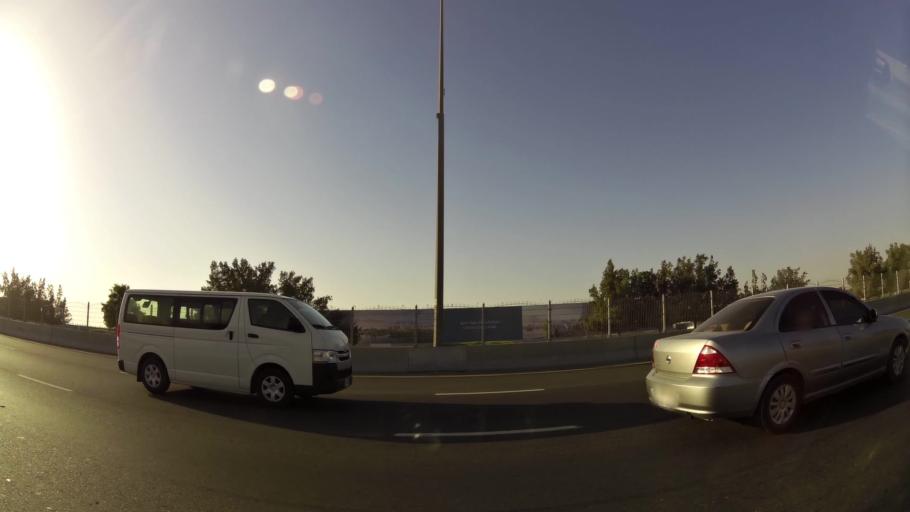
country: AE
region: Ash Shariqah
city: Sharjah
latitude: 25.1856
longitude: 55.3556
